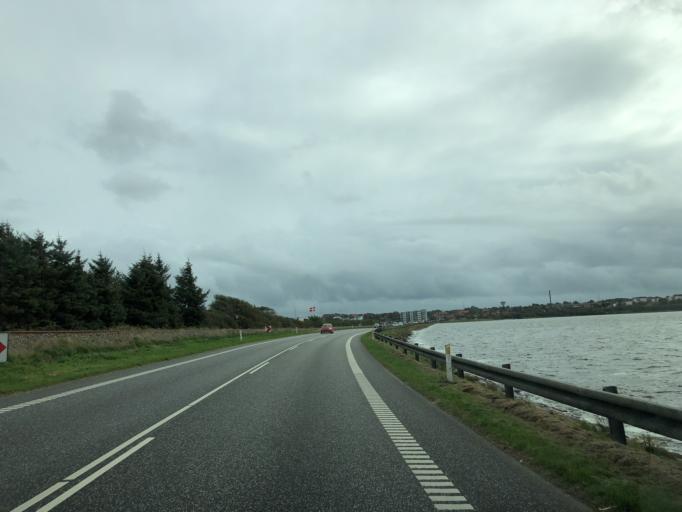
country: DK
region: Central Jutland
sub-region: Struer Kommune
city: Struer
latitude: 56.5029
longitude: 8.5807
